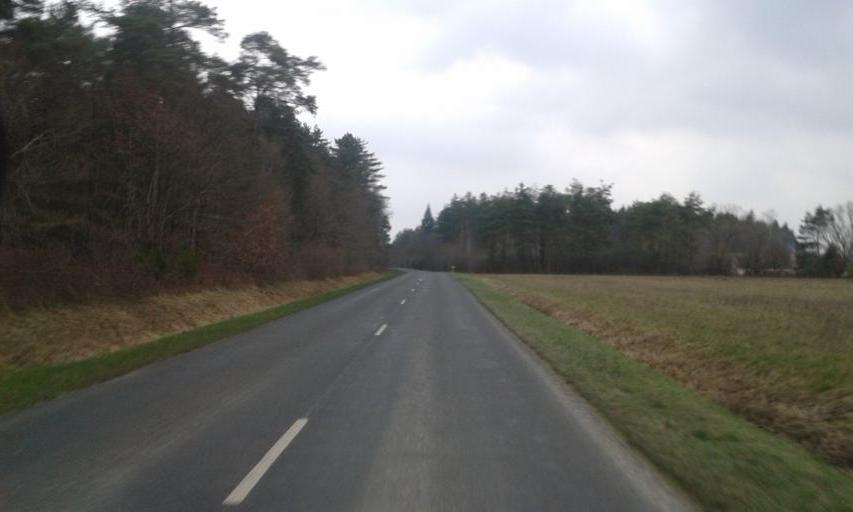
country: FR
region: Centre
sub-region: Departement du Loir-et-Cher
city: Dhuizon
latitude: 47.5973
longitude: 1.6601
